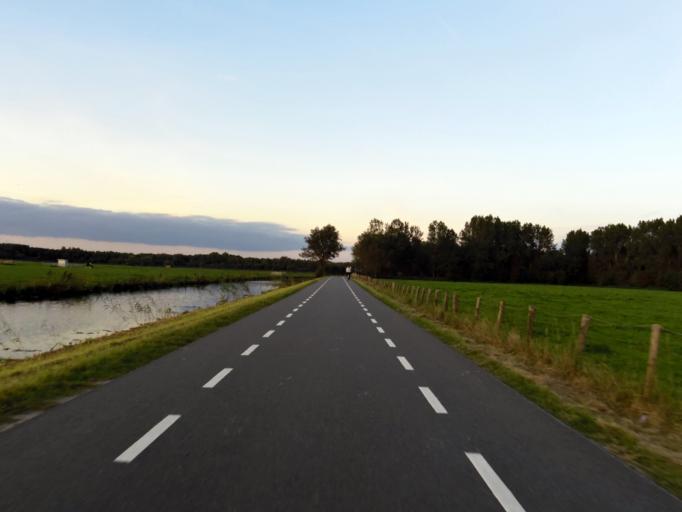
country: NL
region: South Holland
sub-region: Gemeente Wassenaar
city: Wassenaar
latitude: 52.1556
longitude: 4.4191
